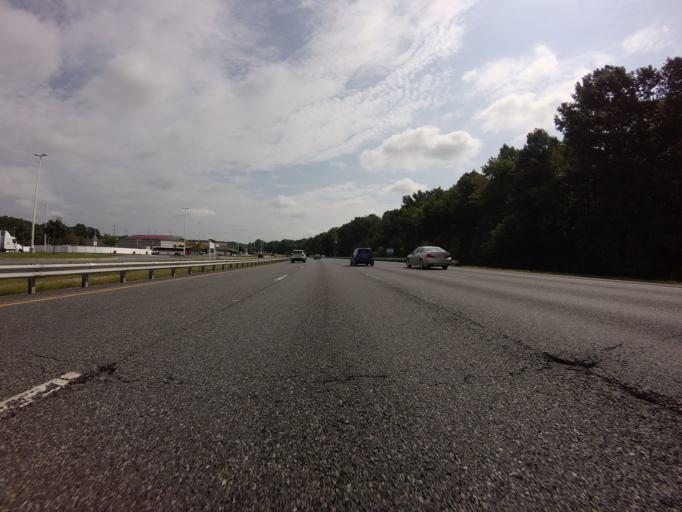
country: US
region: Delaware
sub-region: New Castle County
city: Brookside
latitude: 39.6604
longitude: -75.6924
